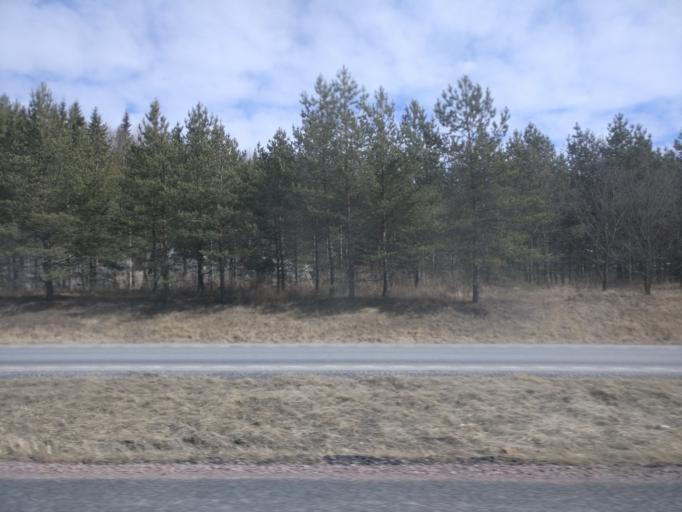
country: FI
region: Pirkanmaa
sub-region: Tampere
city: Tampere
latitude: 61.4645
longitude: 23.7701
